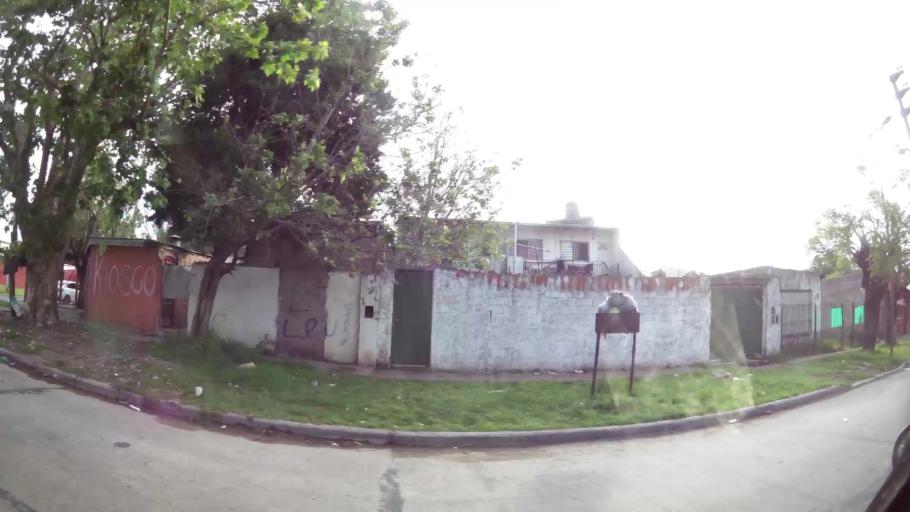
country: AR
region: Buenos Aires
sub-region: Partido de Quilmes
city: Quilmes
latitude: -34.7472
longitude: -58.2527
